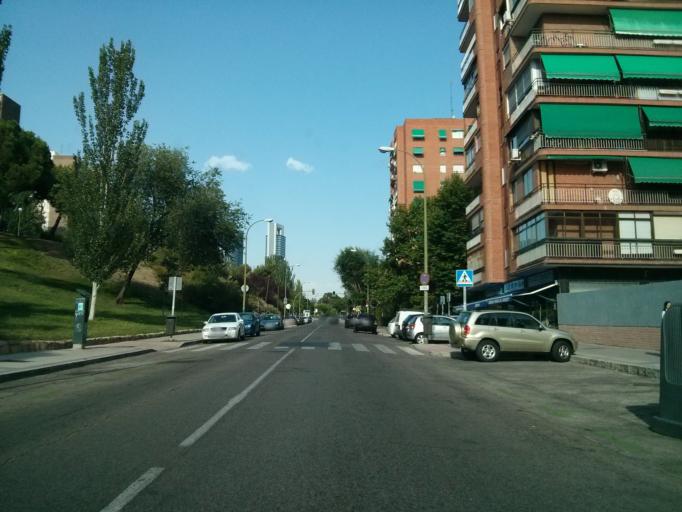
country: ES
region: Madrid
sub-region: Provincia de Madrid
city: Tetuan de las Victorias
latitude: 40.4726
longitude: -3.7068
